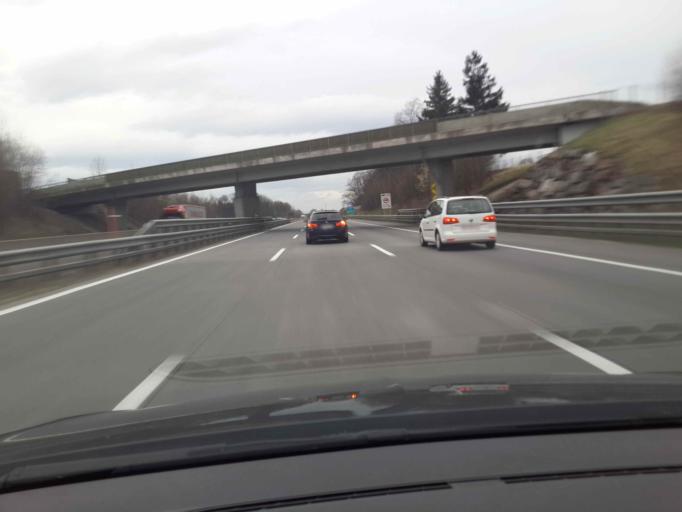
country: AT
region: Lower Austria
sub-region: Politischer Bezirk Amstetten
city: Amstetten
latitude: 48.1417
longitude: 14.8492
